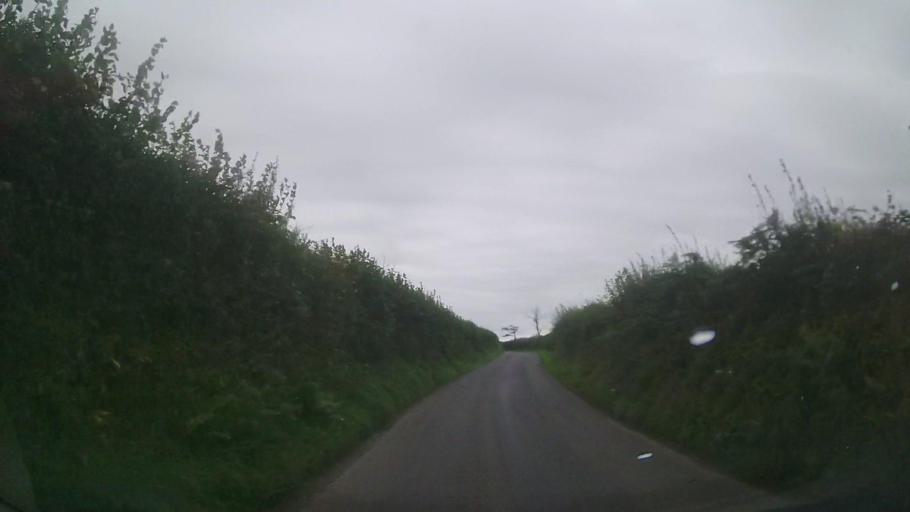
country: GB
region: Wales
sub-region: Carmarthenshire
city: Whitland
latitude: 51.7490
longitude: -4.6120
